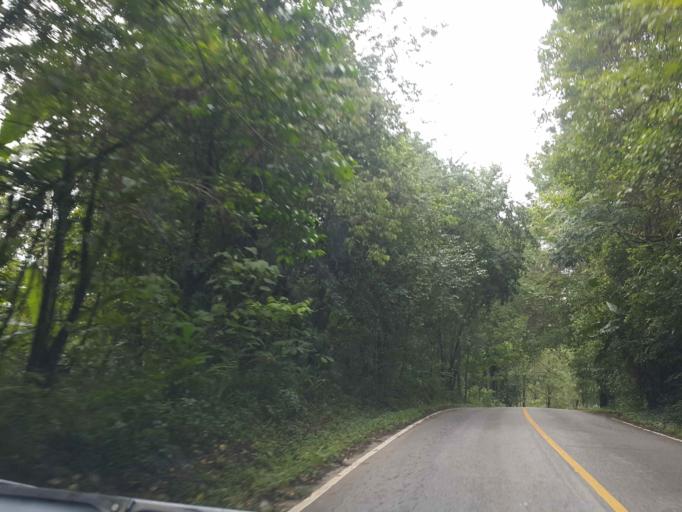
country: TH
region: Chiang Mai
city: Mae Chaem
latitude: 18.5125
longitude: 98.4772
